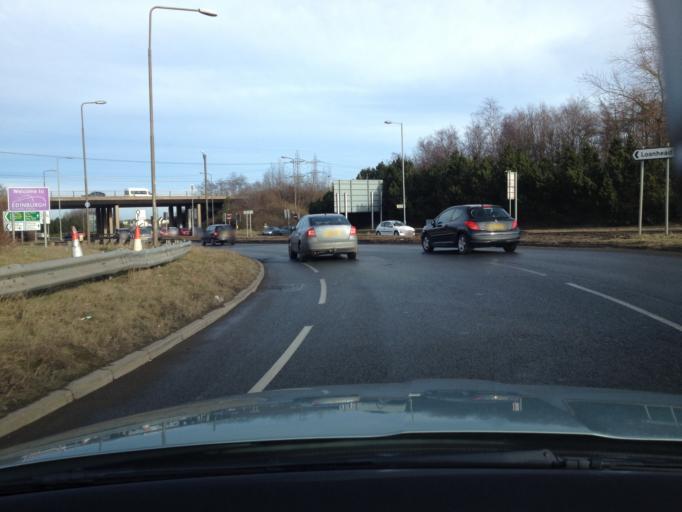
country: GB
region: Scotland
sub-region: Midlothian
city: Loanhead
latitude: 55.8888
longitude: -3.1632
